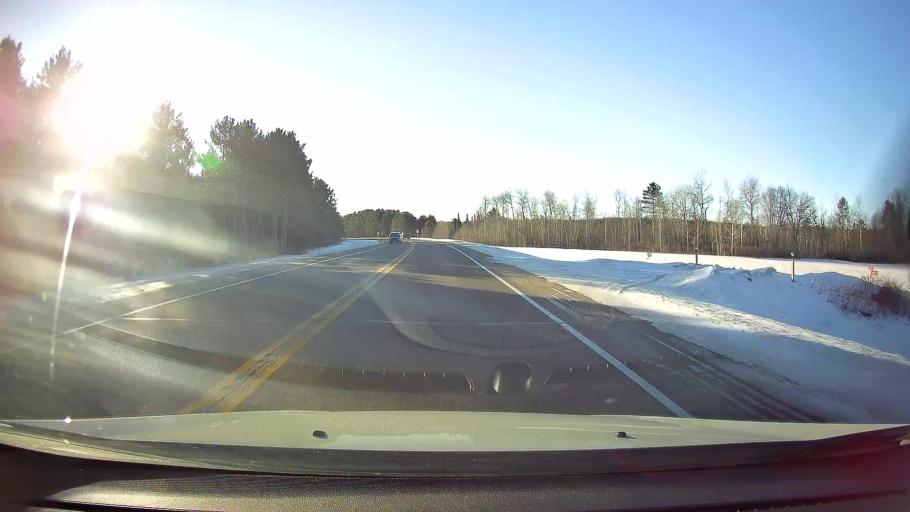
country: US
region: Wisconsin
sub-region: Sawyer County
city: Hayward
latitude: 45.9924
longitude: -91.5933
